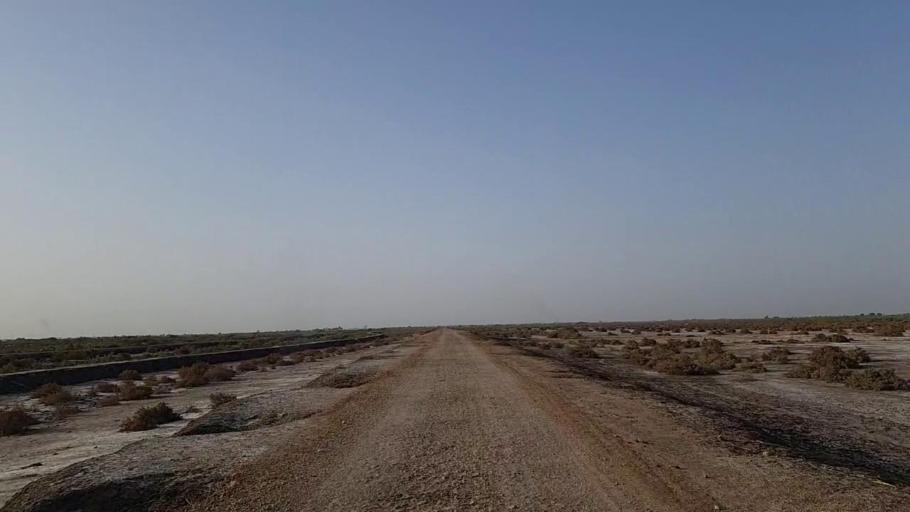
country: PK
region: Sindh
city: Jati
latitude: 24.3547
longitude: 68.1483
